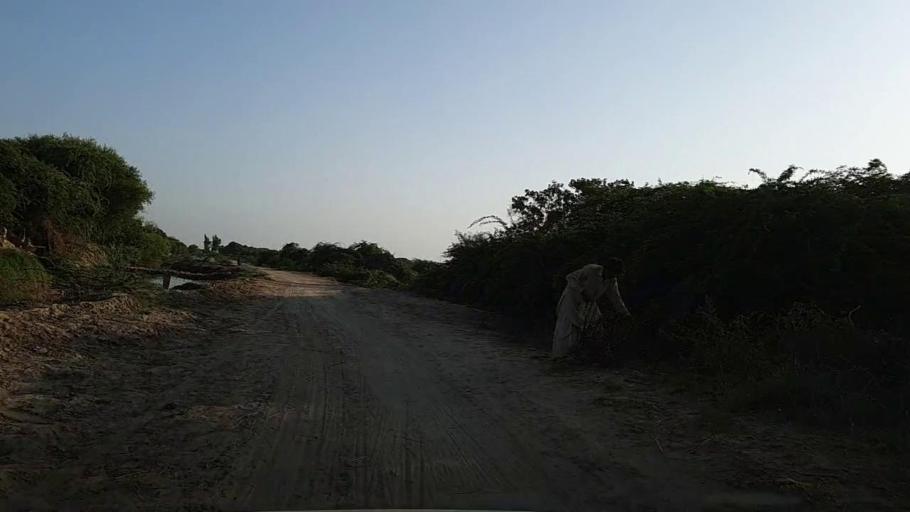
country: PK
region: Sindh
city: Kario
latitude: 24.7254
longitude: 68.6675
